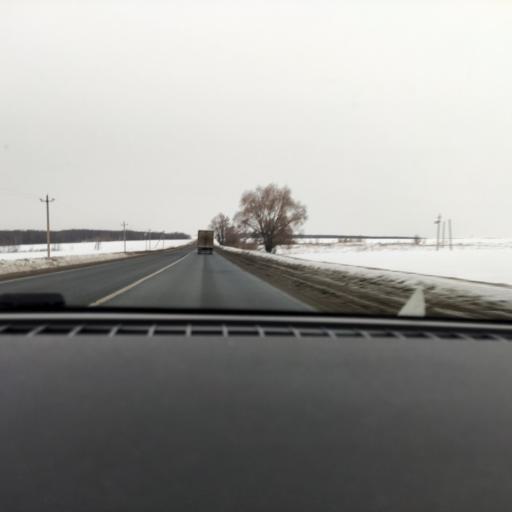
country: RU
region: Samara
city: Petra-Dubrava
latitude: 53.3128
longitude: 50.4568
